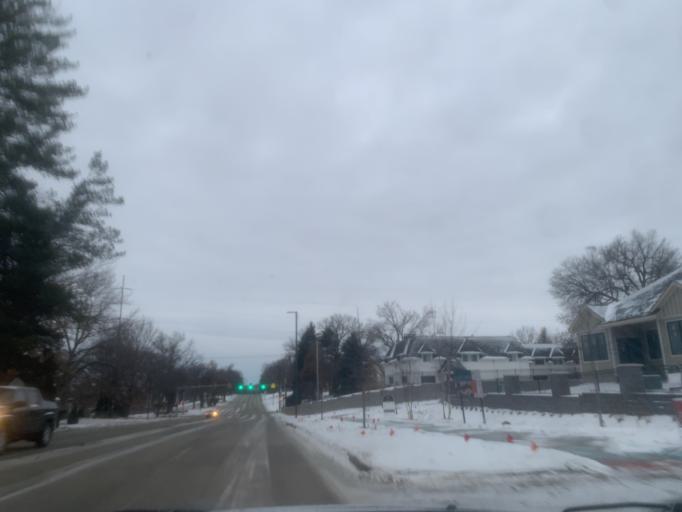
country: US
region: Nebraska
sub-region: Douglas County
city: Ralston
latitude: 41.2500
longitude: -96.0527
